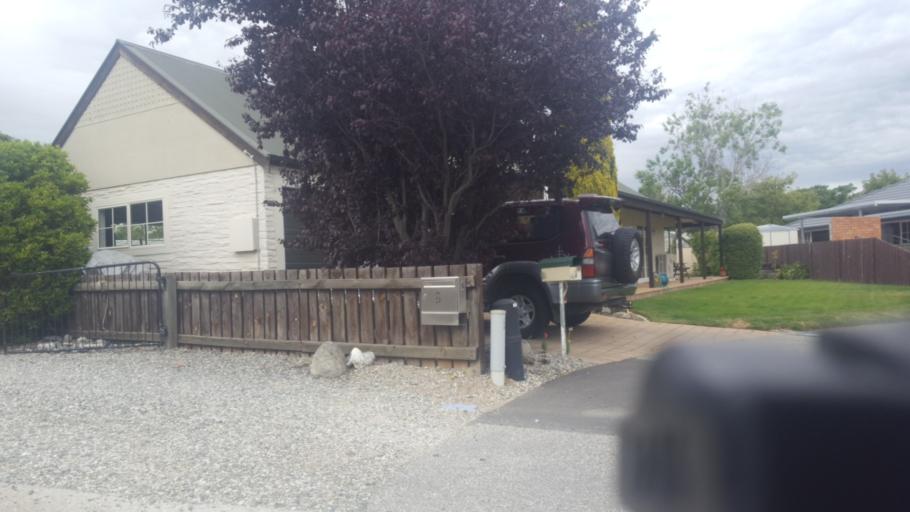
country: NZ
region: Otago
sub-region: Queenstown-Lakes District
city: Wanaka
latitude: -45.0472
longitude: 169.1967
